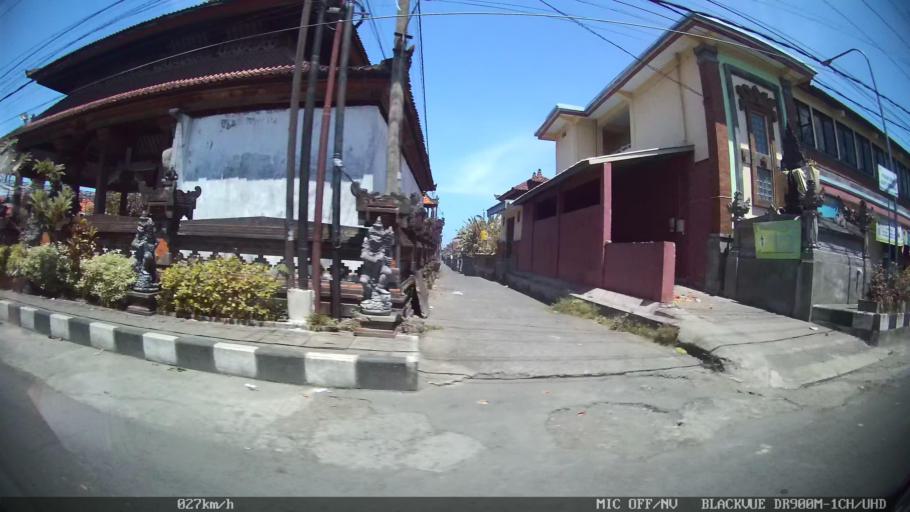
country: ID
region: Bali
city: Banjar Pasekan
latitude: -8.5763
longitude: 115.3246
